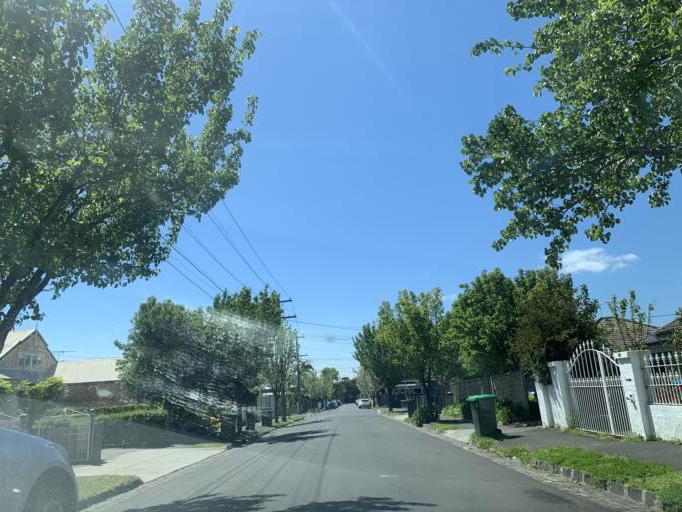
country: AU
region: Victoria
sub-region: Bayside
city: North Brighton
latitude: -37.9114
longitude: 145.0109
